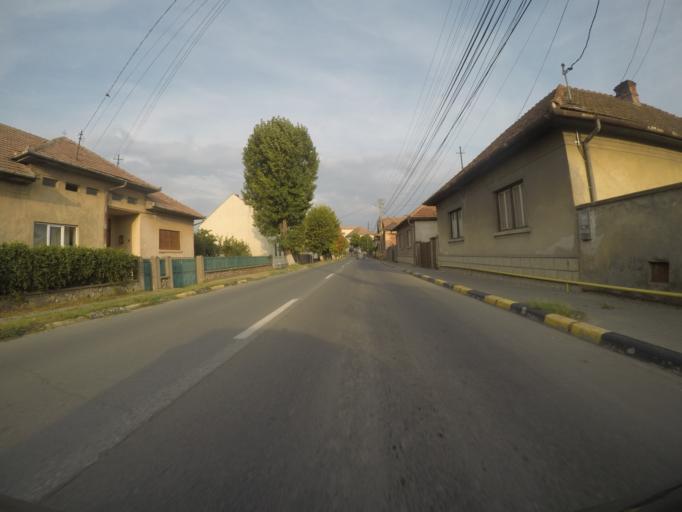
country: RO
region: Alba
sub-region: Municipiul Sebes
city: Sebes
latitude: 45.9553
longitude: 23.5698
